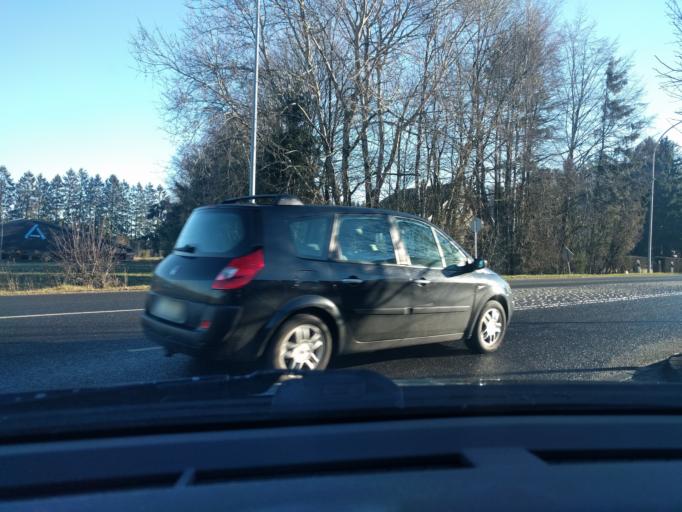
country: LU
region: Diekirch
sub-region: Canton de Clervaux
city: Troisvierges
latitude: 50.1818
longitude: 6.0229
